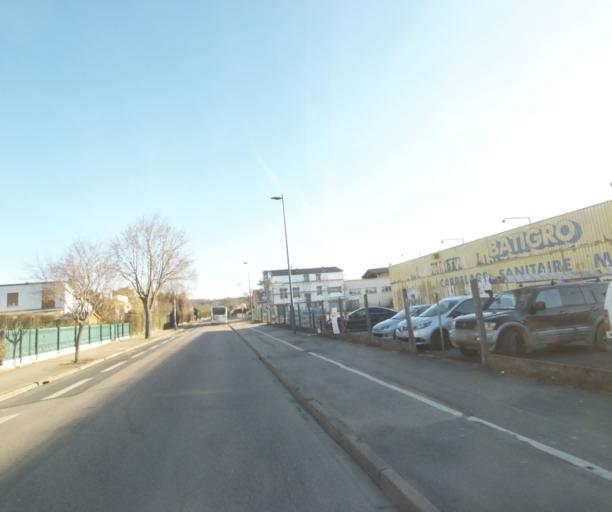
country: FR
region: Lorraine
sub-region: Departement de Meurthe-et-Moselle
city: Seichamps
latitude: 48.7105
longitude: 6.2537
